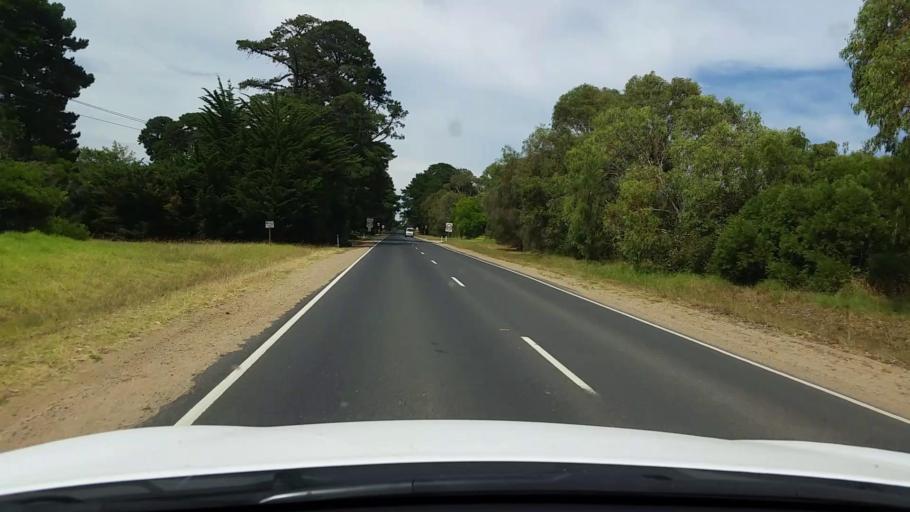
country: AU
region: Victoria
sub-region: Mornington Peninsula
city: Merricks
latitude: -38.4636
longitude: 145.0210
